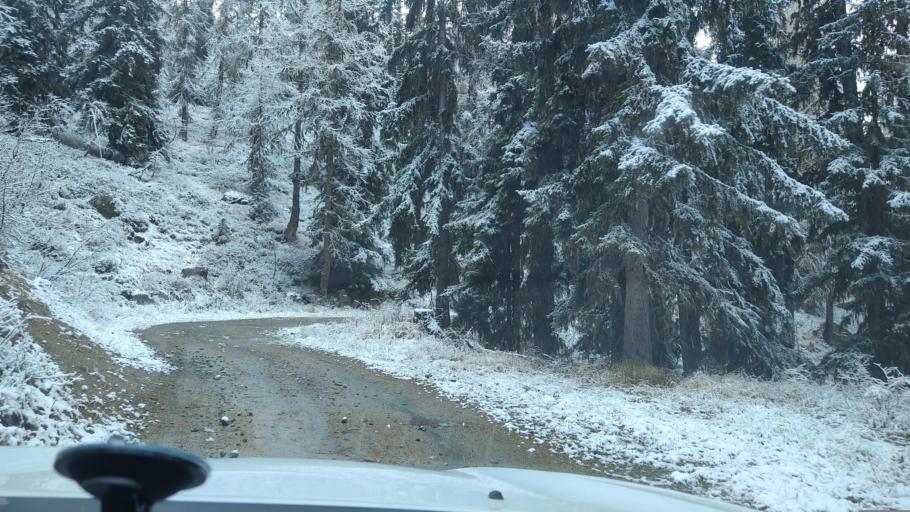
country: FR
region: Rhone-Alpes
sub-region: Departement de la Savoie
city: Seez
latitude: 45.5940
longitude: 6.8072
